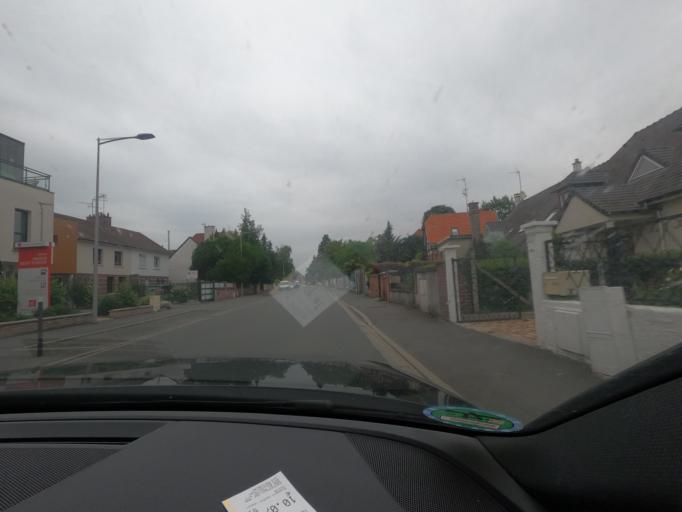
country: FR
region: Picardie
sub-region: Departement de la Somme
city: Amiens
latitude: 49.8751
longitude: 2.3065
